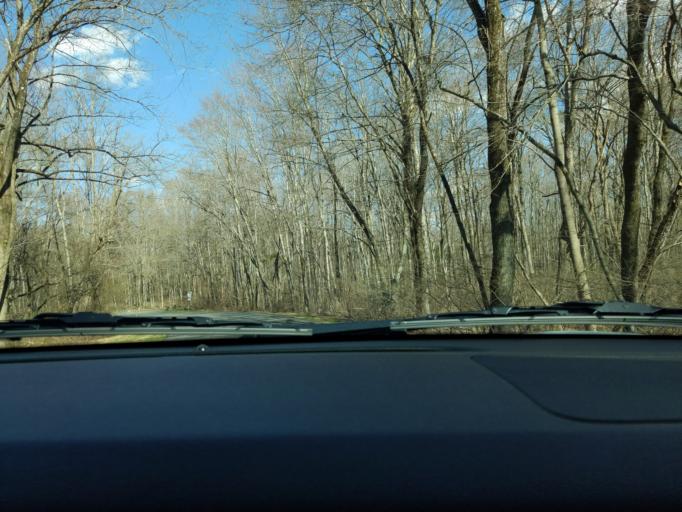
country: US
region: Pennsylvania
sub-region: Bucks County
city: Richlandtown
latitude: 40.4757
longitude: -75.2697
